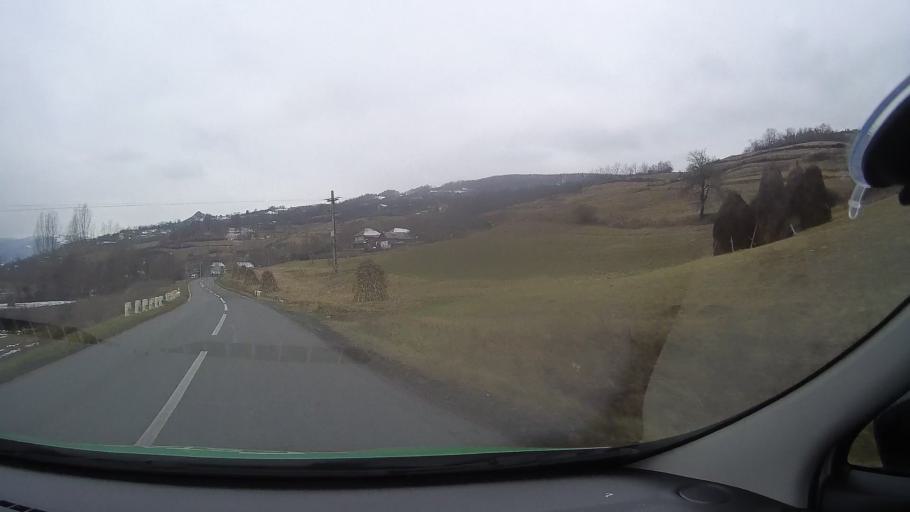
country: RO
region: Alba
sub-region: Comuna Metes
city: Metes
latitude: 46.1051
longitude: 23.4386
